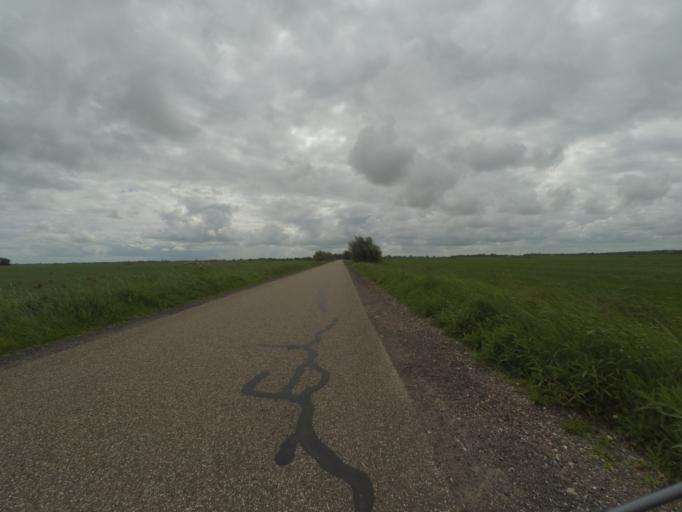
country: NL
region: Friesland
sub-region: Gemeente Kollumerland en Nieuwkruisland
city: Kollumerzwaag
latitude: 53.3146
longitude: 6.0897
